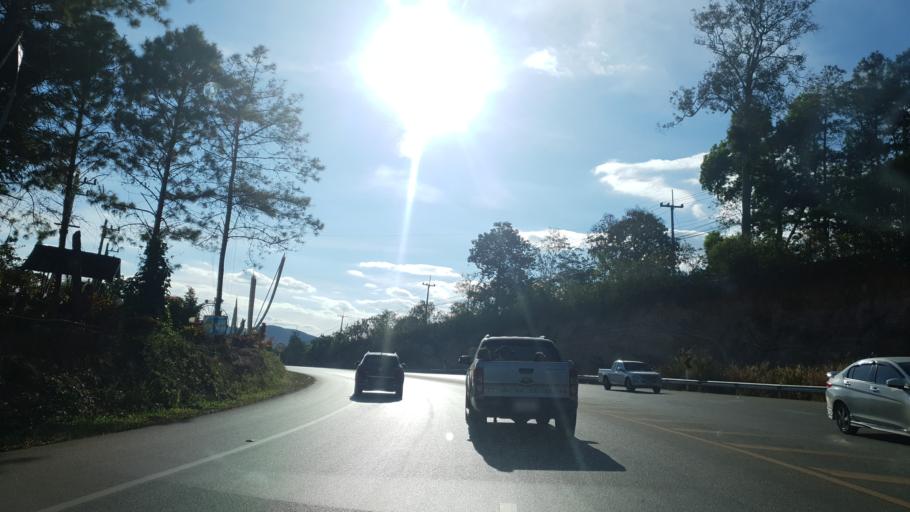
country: TH
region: Loei
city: Phu Ruea
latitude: 17.4583
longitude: 101.3793
